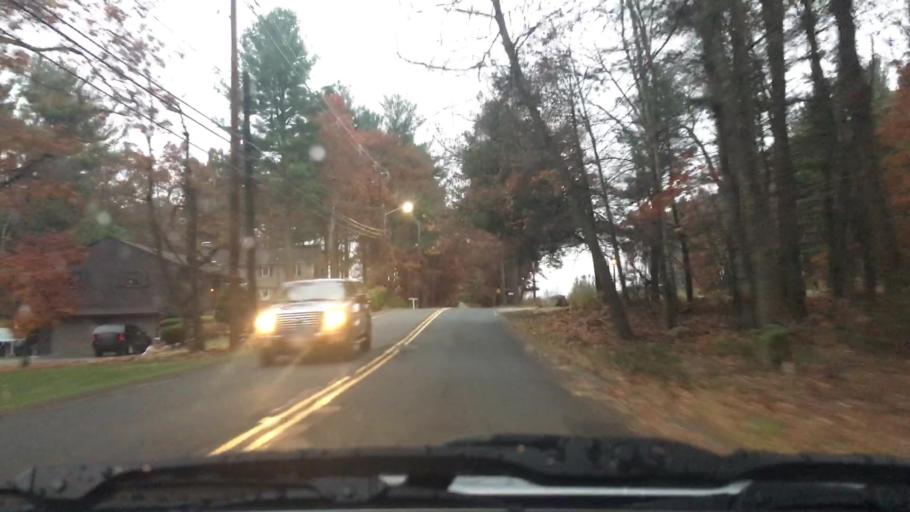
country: US
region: Massachusetts
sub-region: Hampden County
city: Westfield
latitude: 42.1140
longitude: -72.7858
